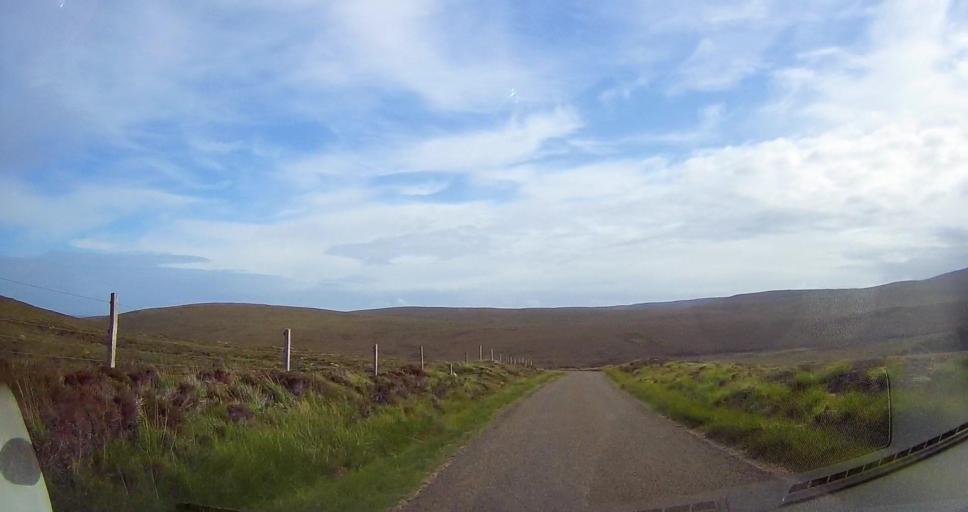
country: GB
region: Scotland
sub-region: Orkney Islands
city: Stromness
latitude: 58.8771
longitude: -3.2467
